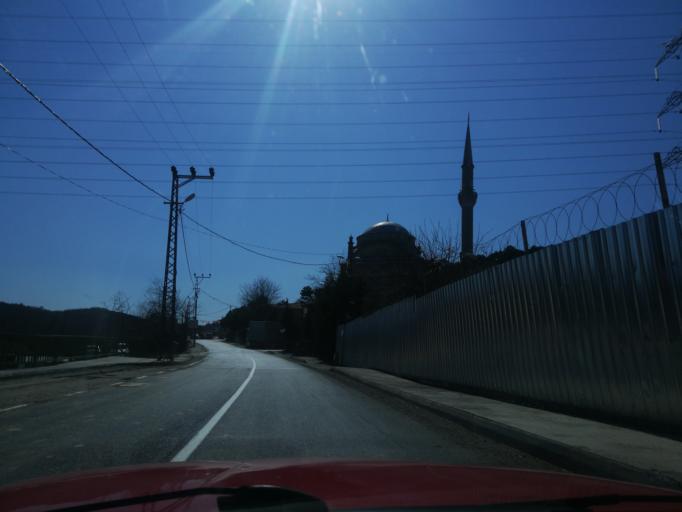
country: TR
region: Istanbul
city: Mahmut Sevket Pasa
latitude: 41.1289
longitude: 29.1605
